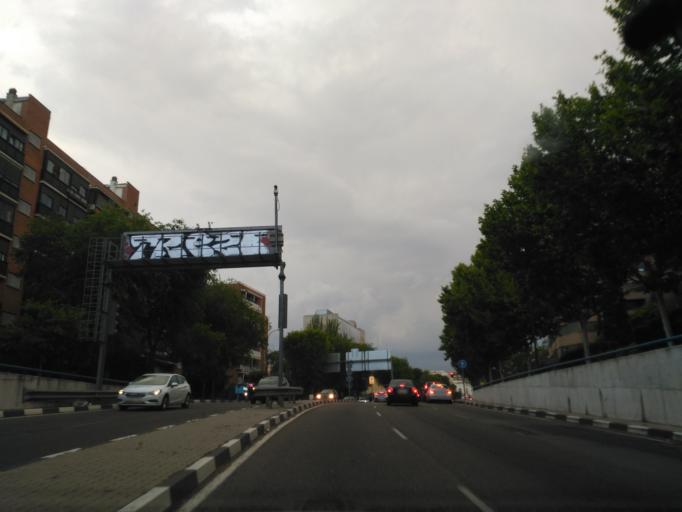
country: ES
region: Madrid
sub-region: Provincia de Madrid
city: Chamartin
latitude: 40.4586
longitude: -3.6704
